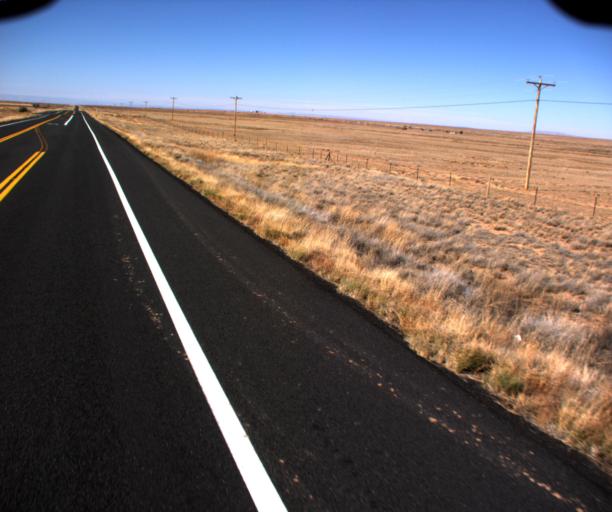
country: US
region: Arizona
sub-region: Coconino County
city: Tuba City
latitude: 35.9970
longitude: -111.0280
